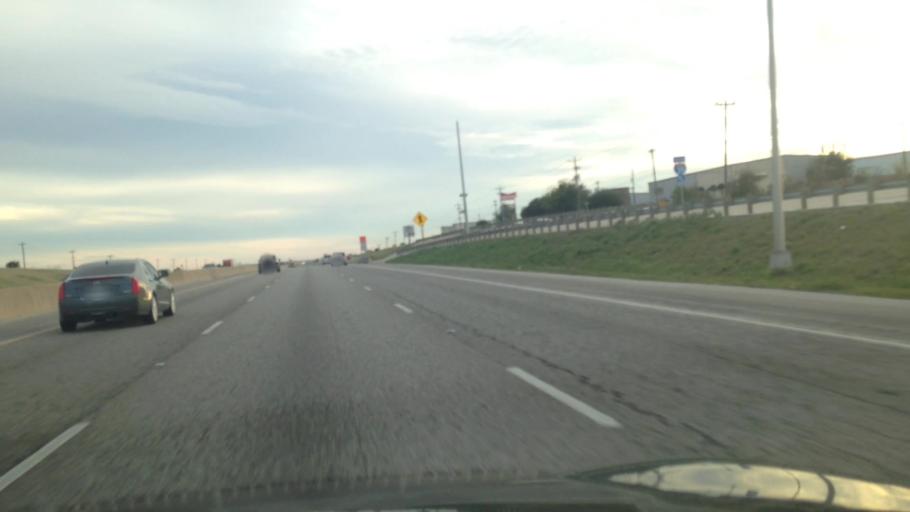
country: US
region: Texas
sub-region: Hays County
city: Buda
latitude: 30.0689
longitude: -97.8292
